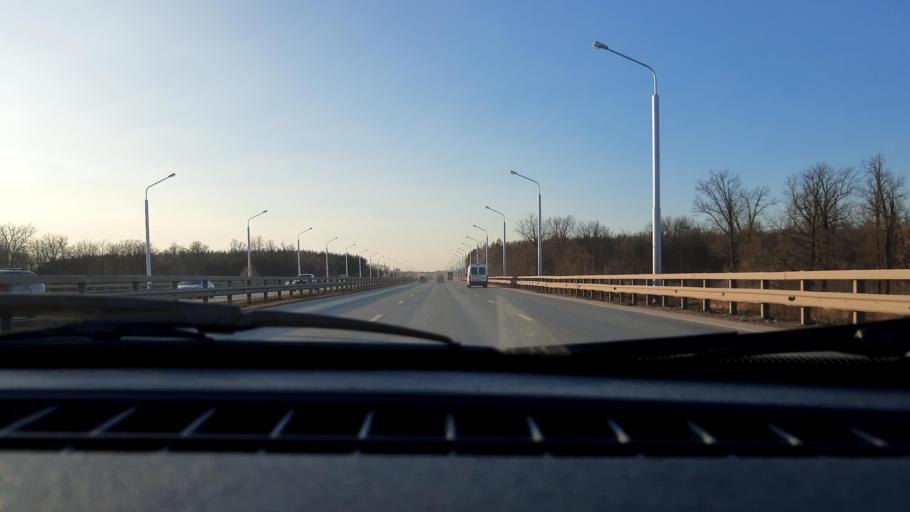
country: RU
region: Bashkortostan
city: Ufa
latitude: 54.7785
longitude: 55.9422
